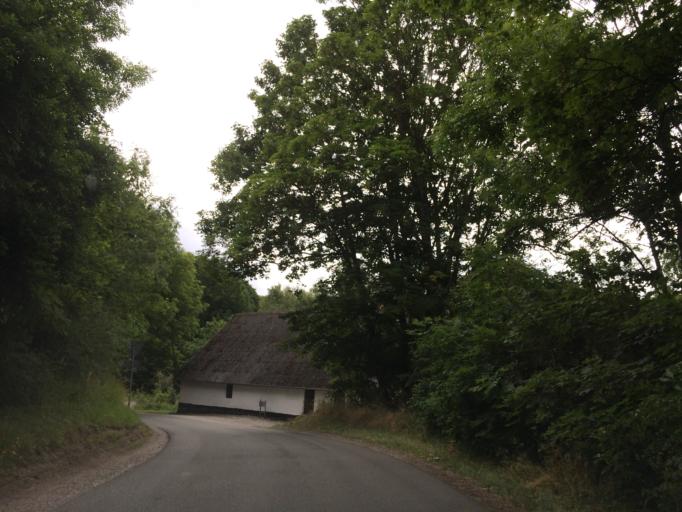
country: DK
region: Central Jutland
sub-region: Syddjurs Kommune
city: Ebeltoft
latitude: 56.2688
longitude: 10.7404
